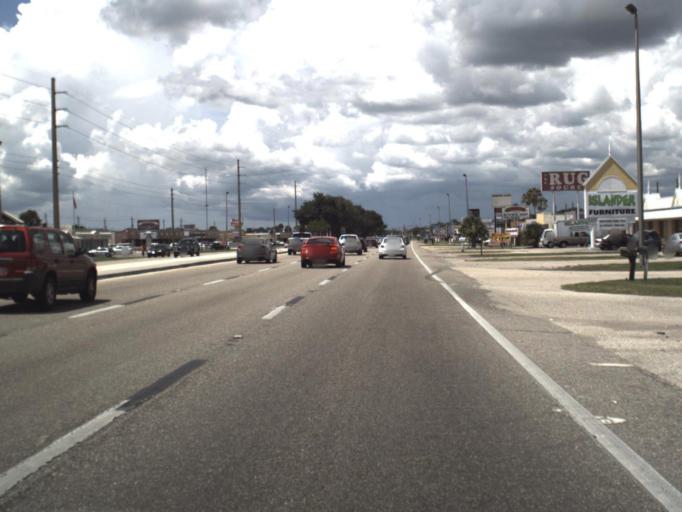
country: US
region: Florida
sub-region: Charlotte County
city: Port Charlotte
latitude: 26.9954
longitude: -82.1170
